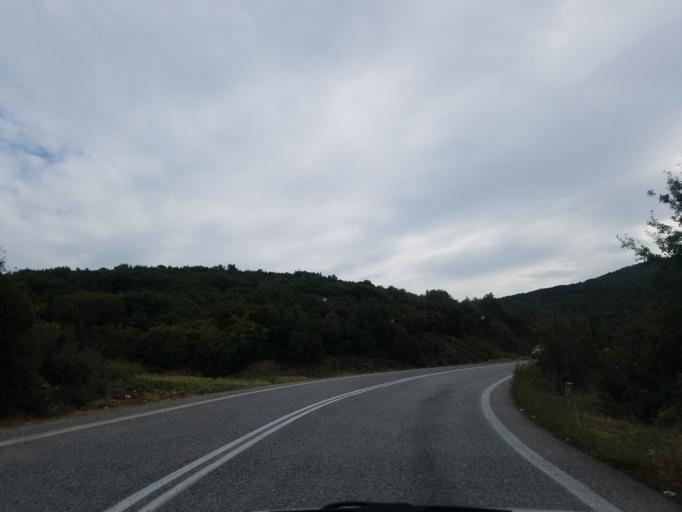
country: GR
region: Central Greece
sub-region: Nomos Fthiotidos
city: Domokos
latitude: 39.1488
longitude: 22.3065
